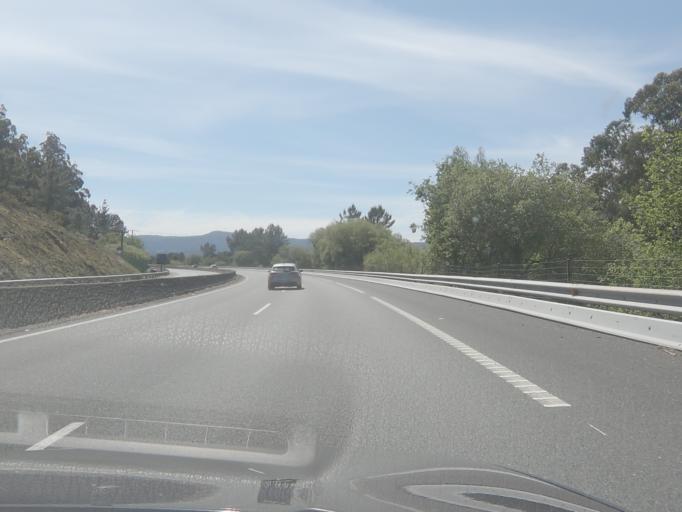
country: ES
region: Galicia
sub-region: Provincia da Coruna
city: Padron
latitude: 42.7966
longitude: -8.6337
